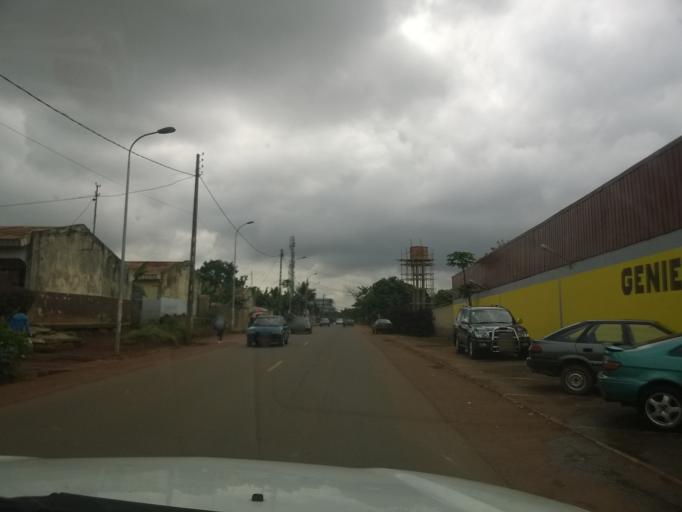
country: CM
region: Centre
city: Yaounde
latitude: 3.8537
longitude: 11.5071
